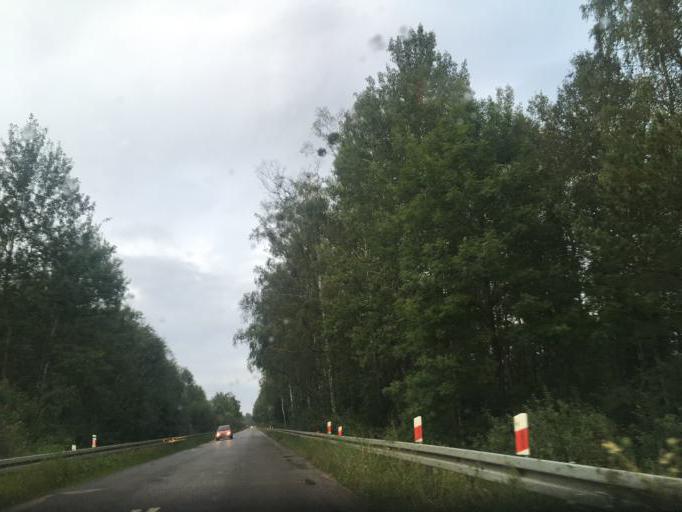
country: PL
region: Podlasie
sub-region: Powiat hajnowski
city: Hajnowka
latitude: 52.8235
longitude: 23.7017
